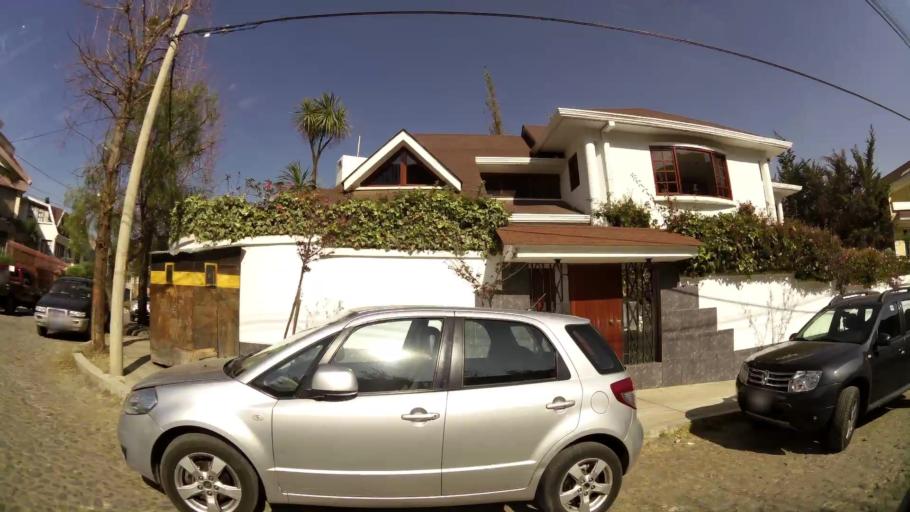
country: BO
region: La Paz
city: La Paz
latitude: -16.5169
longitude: -68.0639
